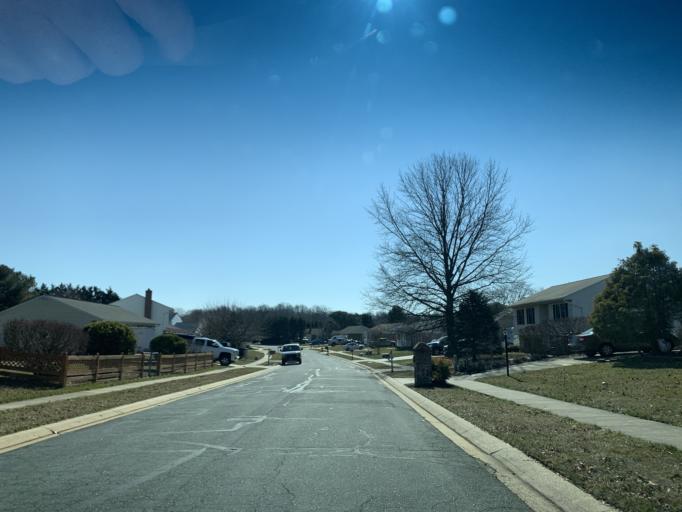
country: US
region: Maryland
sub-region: Harford County
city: South Bel Air
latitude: 39.5420
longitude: -76.2971
